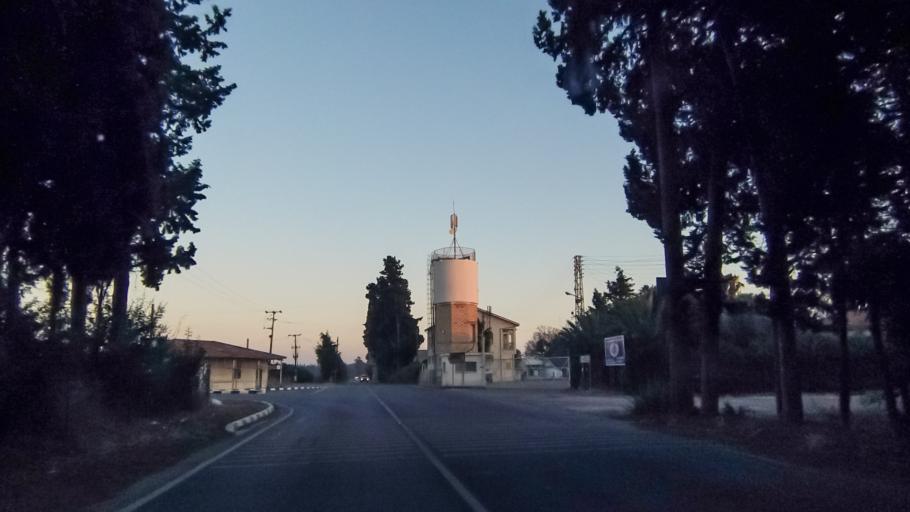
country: CY
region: Larnaka
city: Kolossi
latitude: 34.6377
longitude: 32.9463
